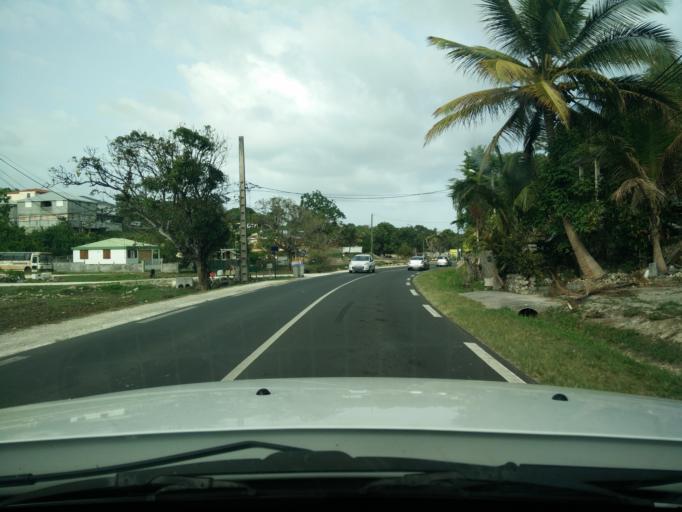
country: GP
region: Guadeloupe
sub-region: Guadeloupe
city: Sainte-Anne
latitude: 16.2179
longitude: -61.4170
